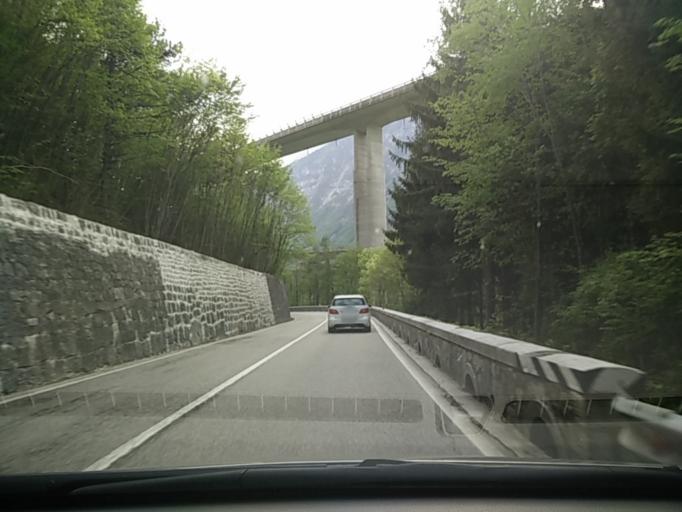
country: IT
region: Veneto
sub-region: Provincia di Belluno
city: Farra d'Alpago
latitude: 46.0699
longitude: 12.3396
